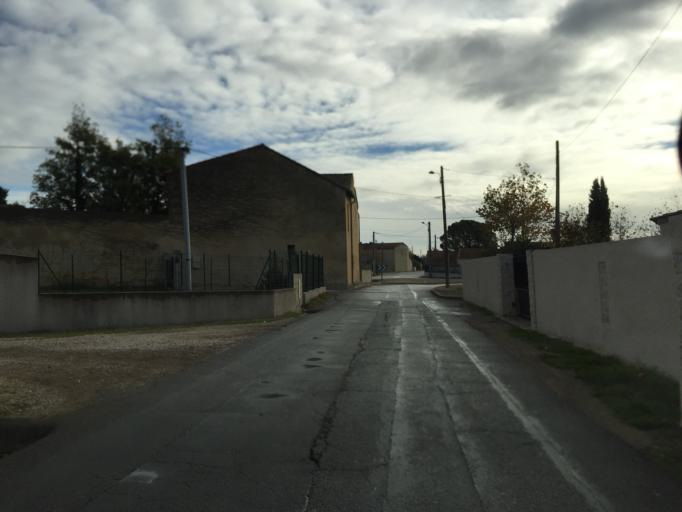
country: FR
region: Provence-Alpes-Cote d'Azur
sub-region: Departement du Vaucluse
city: Sorgues
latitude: 44.0024
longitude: 4.8853
